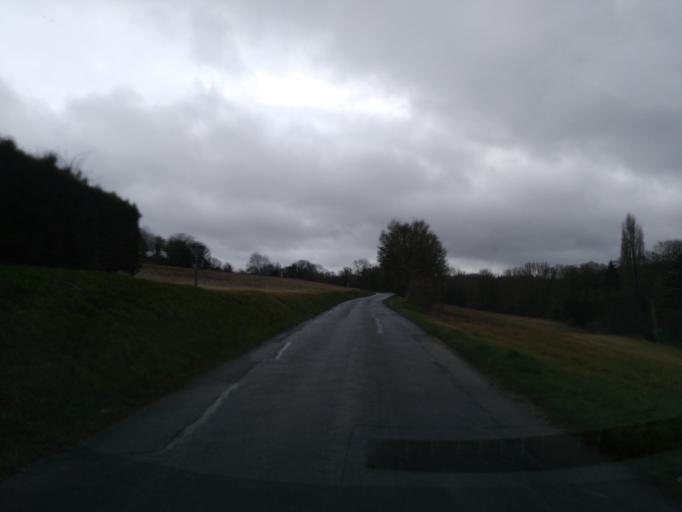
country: FR
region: Ile-de-France
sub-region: Departement des Yvelines
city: Mantes-la-Ville
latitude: 48.9483
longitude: 1.7032
